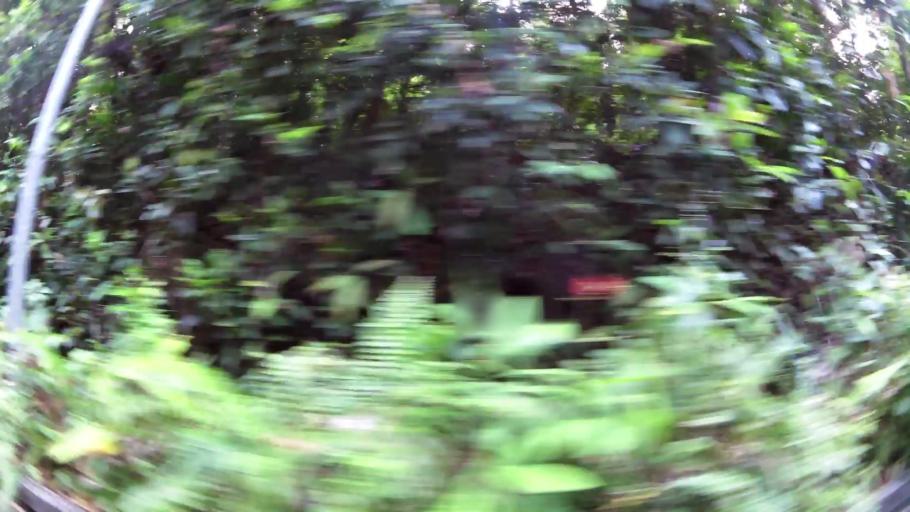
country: SG
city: Singapore
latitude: 1.2576
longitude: 103.8124
